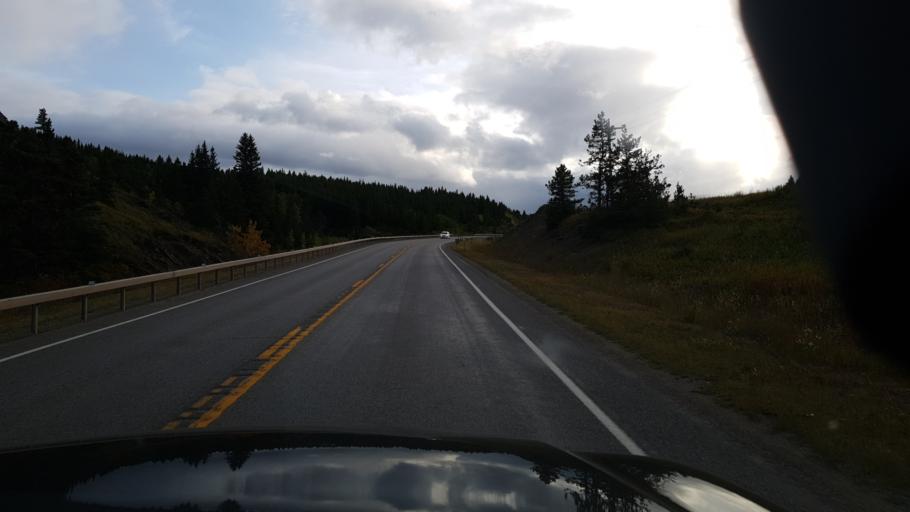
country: US
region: Montana
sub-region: Glacier County
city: South Browning
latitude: 48.3926
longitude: -113.2568
